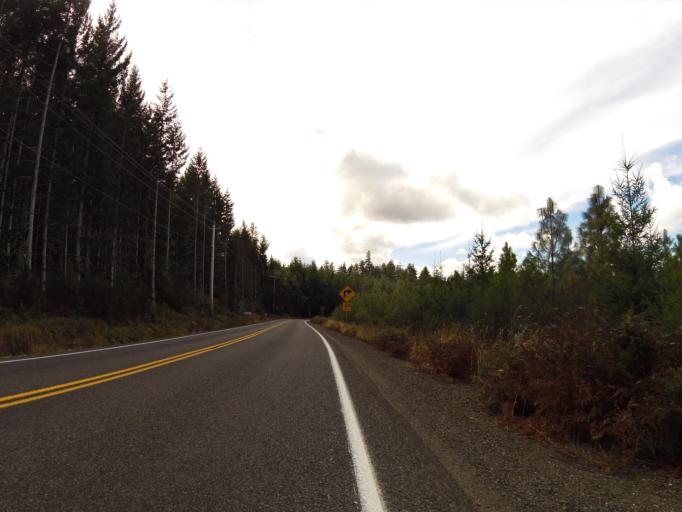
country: US
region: Washington
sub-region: Mason County
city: Shelton
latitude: 47.1475
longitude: -123.0755
